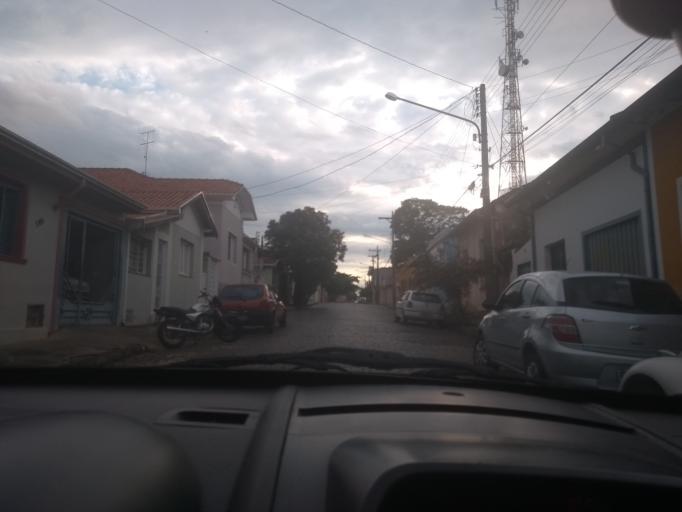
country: BR
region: Sao Paulo
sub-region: Casa Branca
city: Casa Branca
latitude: -21.7748
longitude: -47.0810
